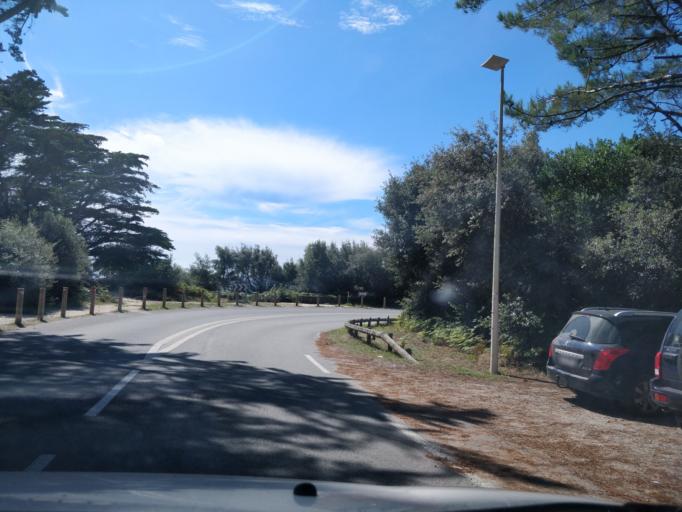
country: FR
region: Brittany
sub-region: Departement du Morbihan
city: Saint-Philibert
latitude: 47.5681
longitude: -2.9994
